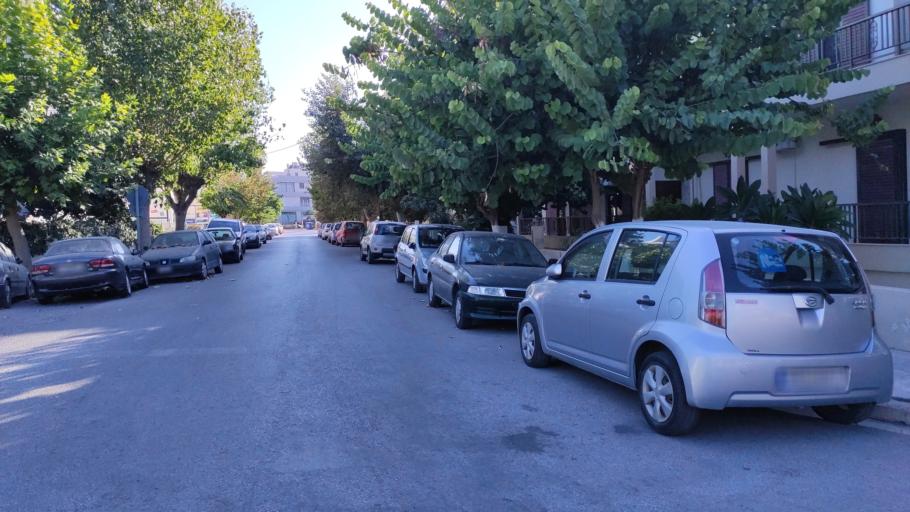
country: GR
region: South Aegean
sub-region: Nomos Dodekanisou
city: Kos
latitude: 36.8970
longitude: 27.2824
